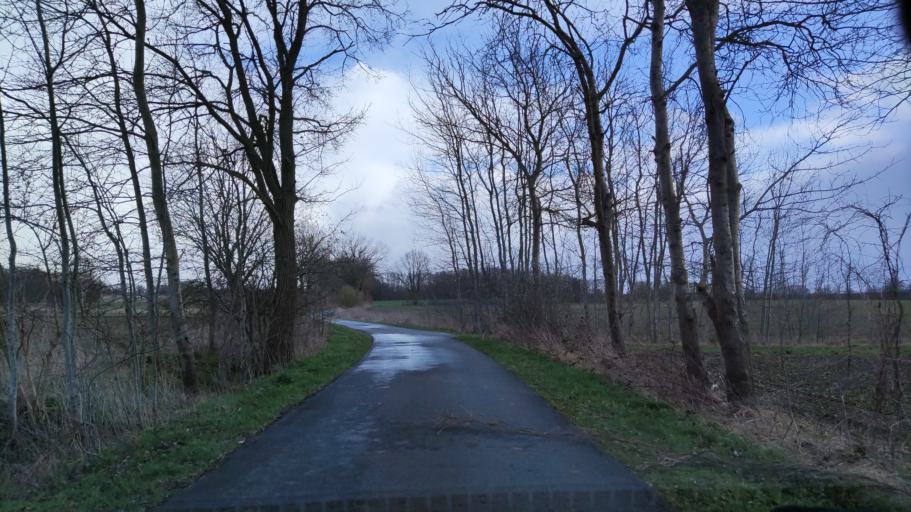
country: DE
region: Lower Saxony
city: Dahlenburg
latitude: 53.1875
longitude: 10.7145
